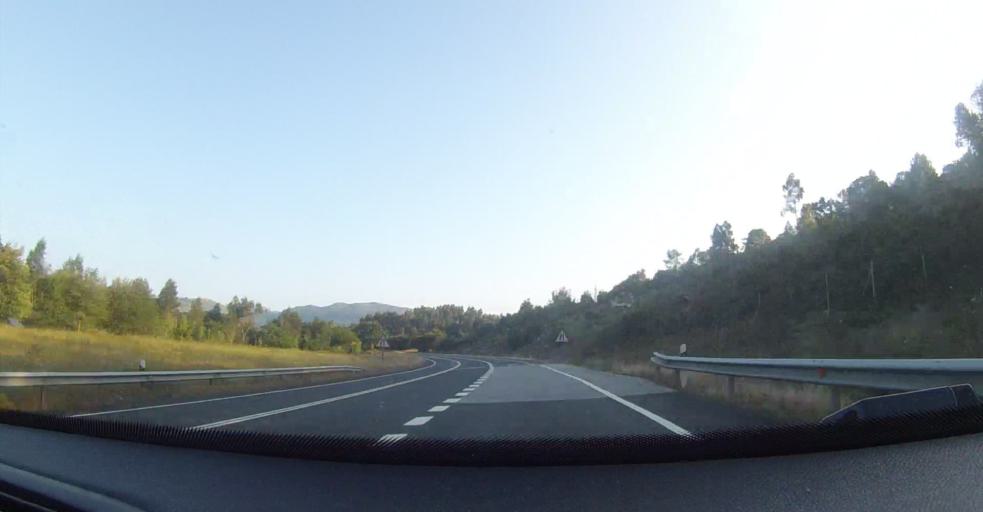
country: ES
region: Cantabria
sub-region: Provincia de Cantabria
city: Ampuero
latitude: 43.3276
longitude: -3.4091
